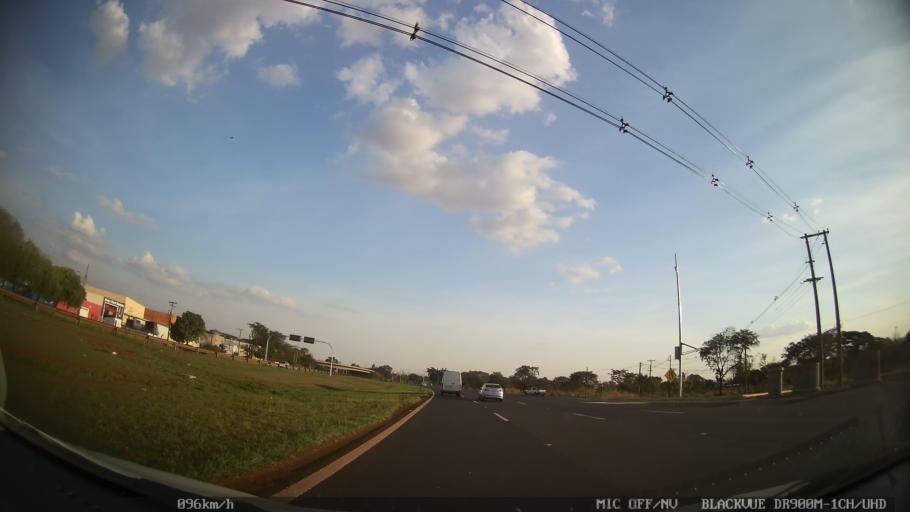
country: BR
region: Sao Paulo
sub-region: Ribeirao Preto
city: Ribeirao Preto
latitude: -21.1175
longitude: -47.7851
